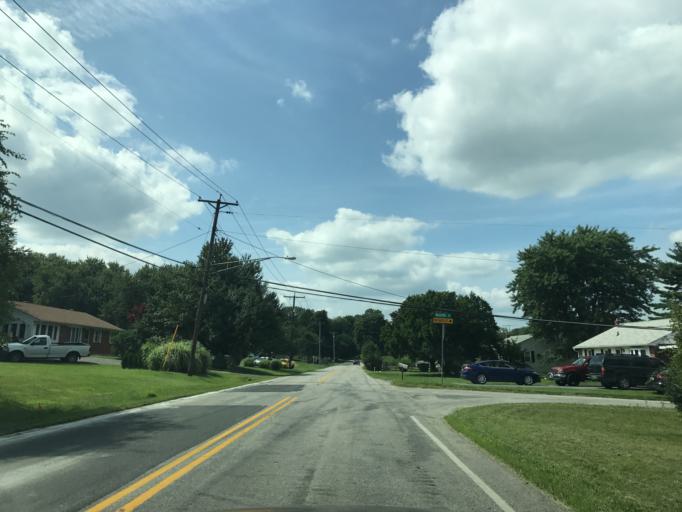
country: US
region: Maryland
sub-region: Harford County
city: South Bel Air
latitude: 39.5625
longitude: -76.3124
